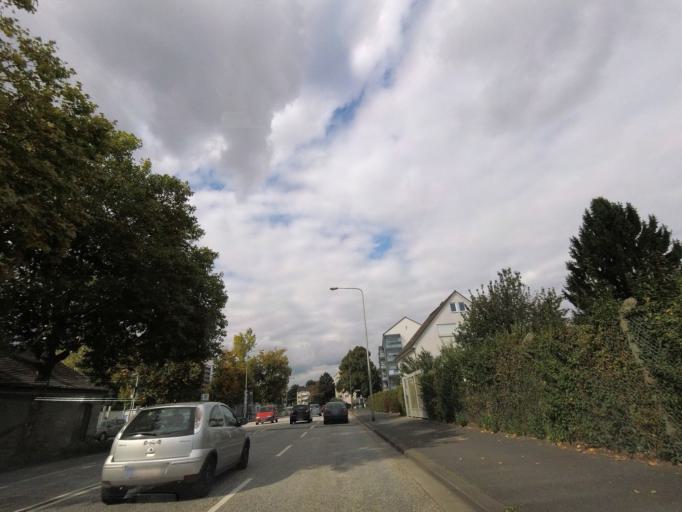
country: DE
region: Hesse
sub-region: Regierungsbezirk Darmstadt
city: Wiesbaden
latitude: 50.0663
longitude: 8.2330
